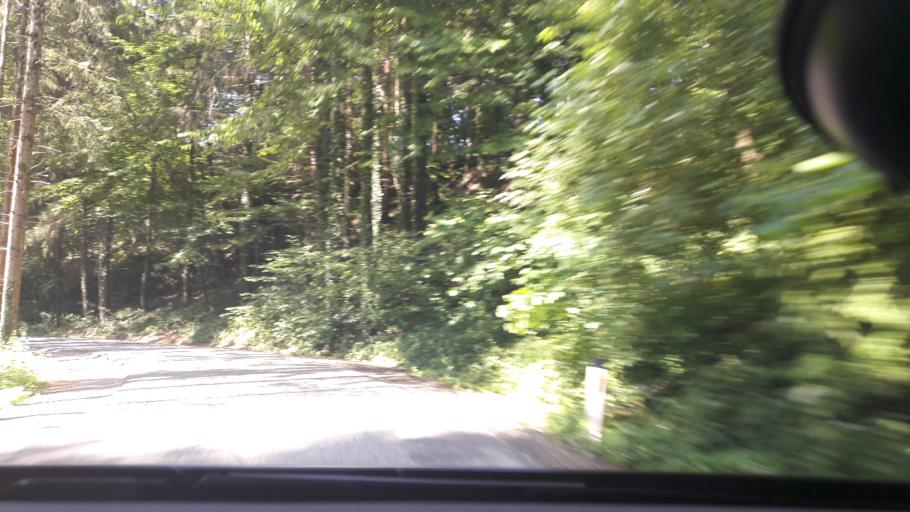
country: AT
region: Styria
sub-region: Politischer Bezirk Voitsberg
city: Sodingberg
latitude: 47.0961
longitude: 15.1851
